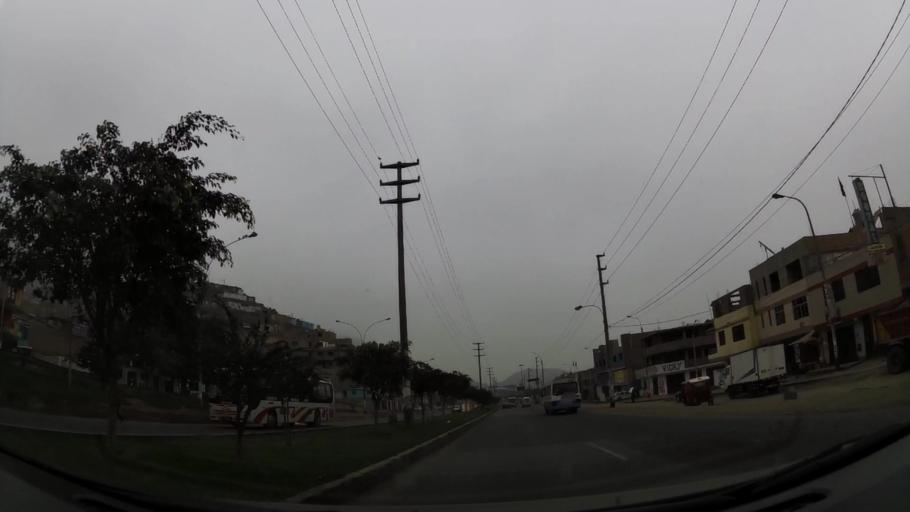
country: PE
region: Lima
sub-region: Lima
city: Urb. Santo Domingo
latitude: -11.8966
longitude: -77.0297
